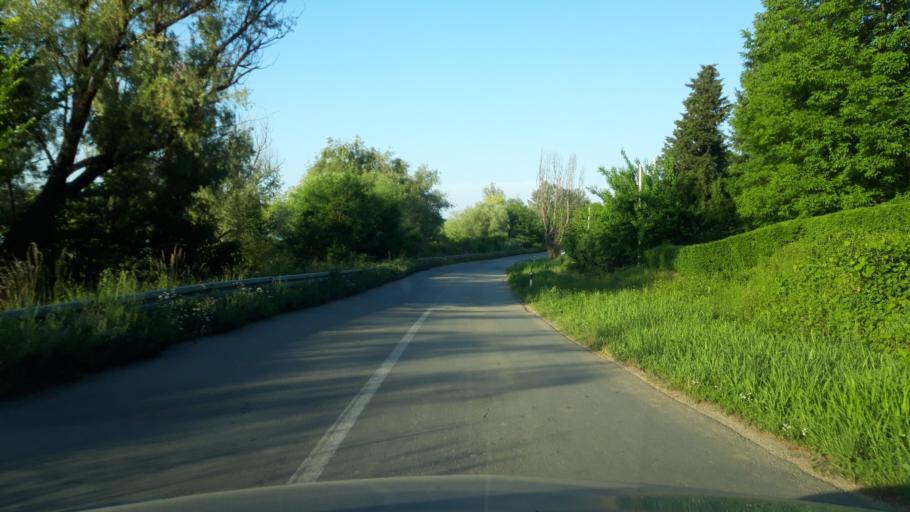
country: RS
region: Autonomna Pokrajina Vojvodina
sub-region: Juznobacki Okrug
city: Beocin
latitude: 45.2186
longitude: 19.6428
